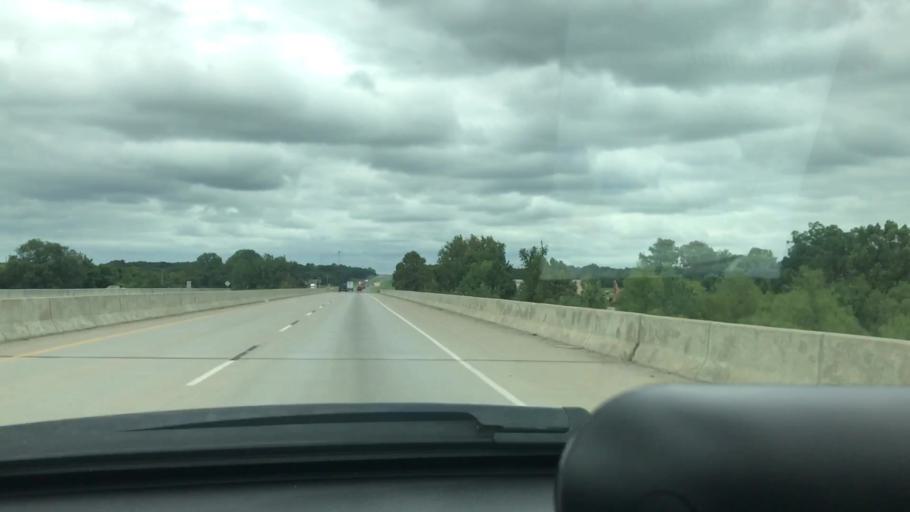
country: US
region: Oklahoma
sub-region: Muskogee County
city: Muskogee
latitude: 35.8097
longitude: -95.4021
